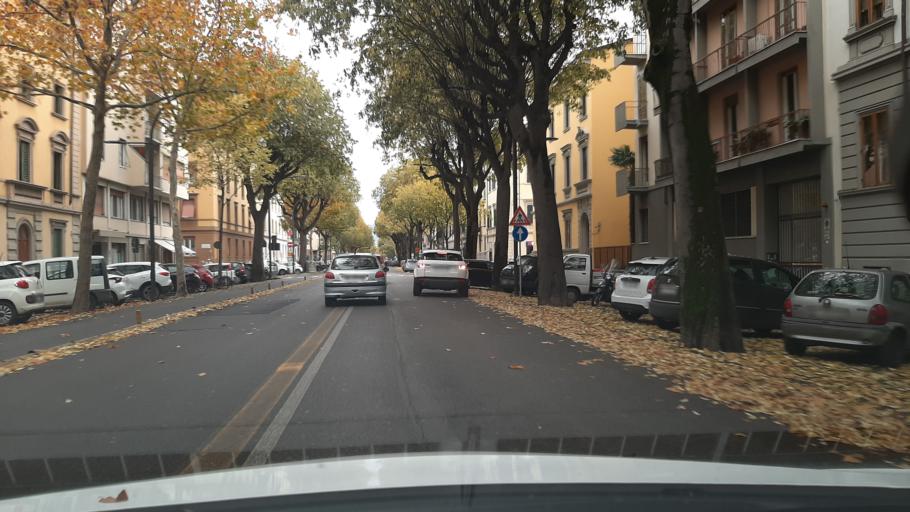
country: IT
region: Tuscany
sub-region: Province of Florence
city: Fiesole
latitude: 43.7824
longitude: 11.2761
